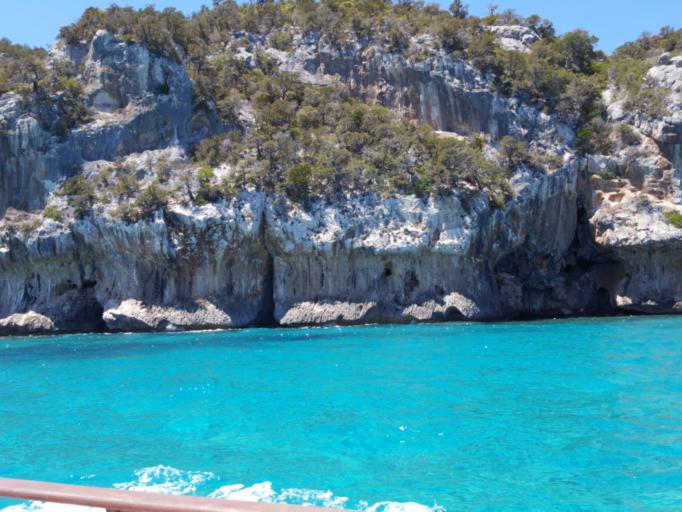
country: IT
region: Sardinia
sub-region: Provincia di Nuoro
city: Cala Gonone
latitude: 40.2502
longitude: 9.6246
